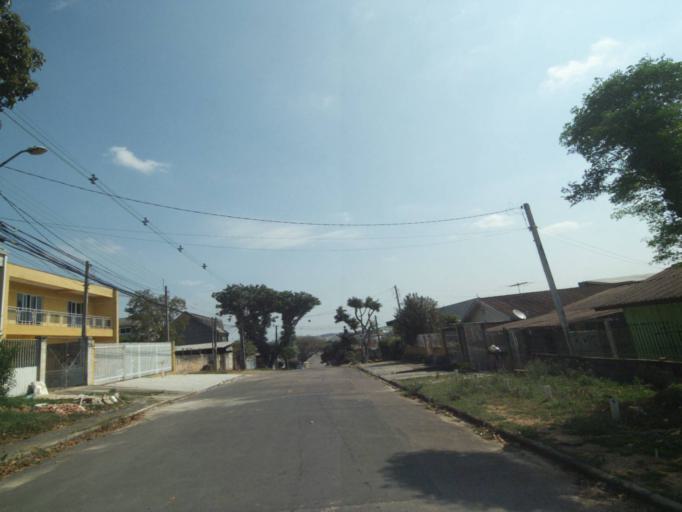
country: BR
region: Parana
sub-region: Curitiba
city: Curitiba
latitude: -25.4852
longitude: -49.3294
